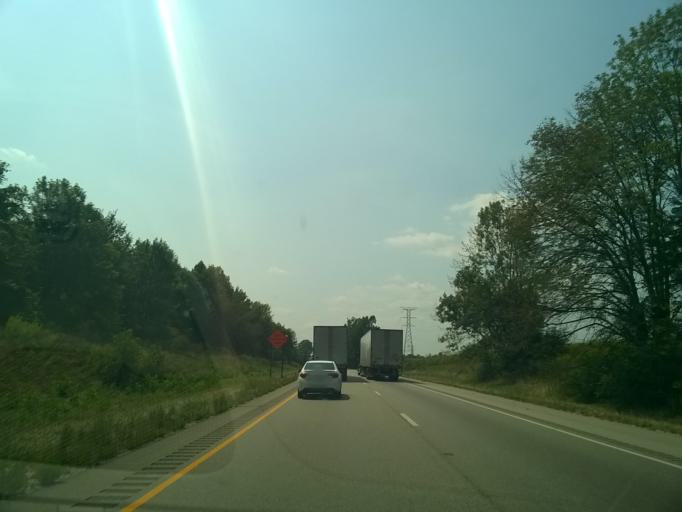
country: US
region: Indiana
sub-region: Vigo County
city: Seelyville
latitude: 39.4405
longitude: -87.2788
